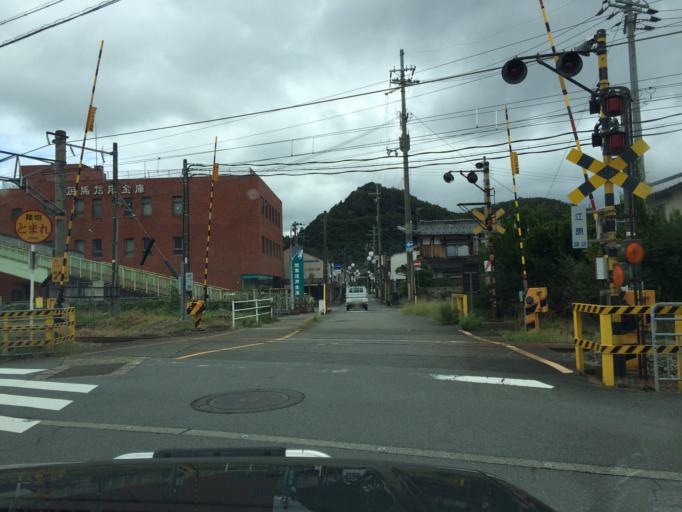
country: JP
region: Hyogo
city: Toyooka
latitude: 35.4672
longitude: 134.7737
